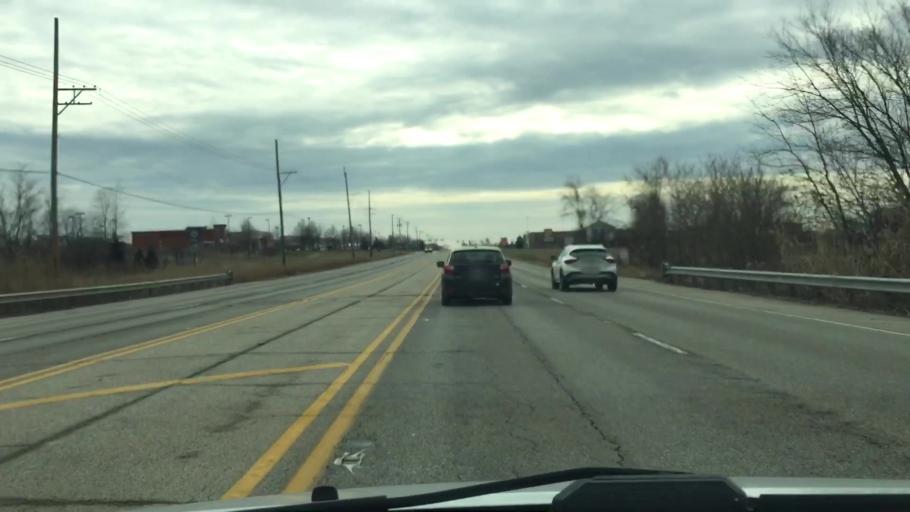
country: US
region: Illinois
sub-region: McHenry County
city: McCullom Lake
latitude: 42.3635
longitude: -88.2673
